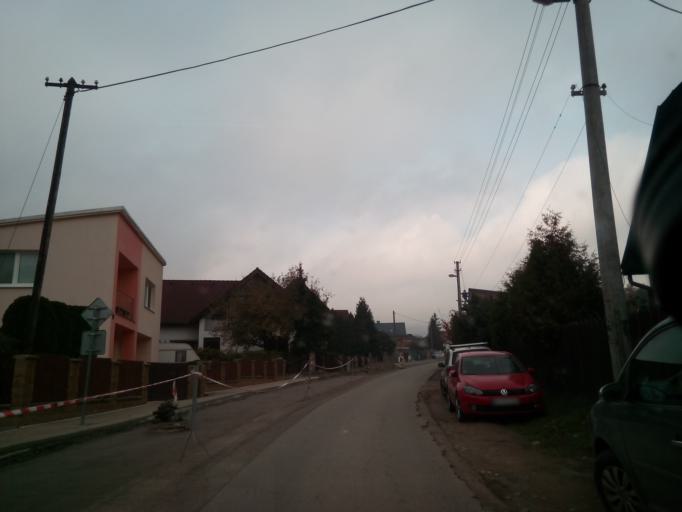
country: SK
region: Kosicky
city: Kosice
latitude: 48.7252
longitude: 21.1446
